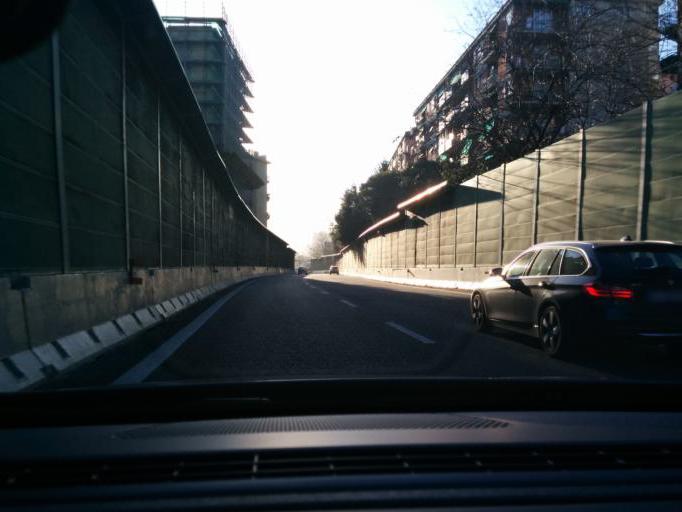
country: IT
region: Liguria
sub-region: Provincia di Genova
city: Mele
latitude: 44.4303
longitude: 8.7724
